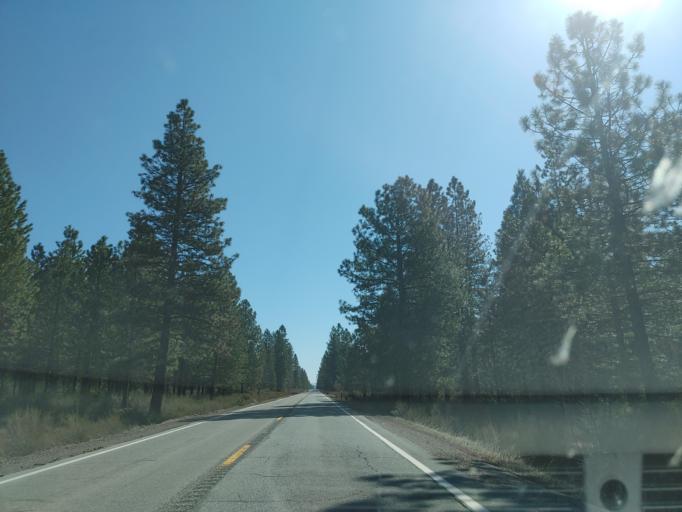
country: US
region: California
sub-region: Siskiyou County
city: McCloud
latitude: 41.2518
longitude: -122.1157
